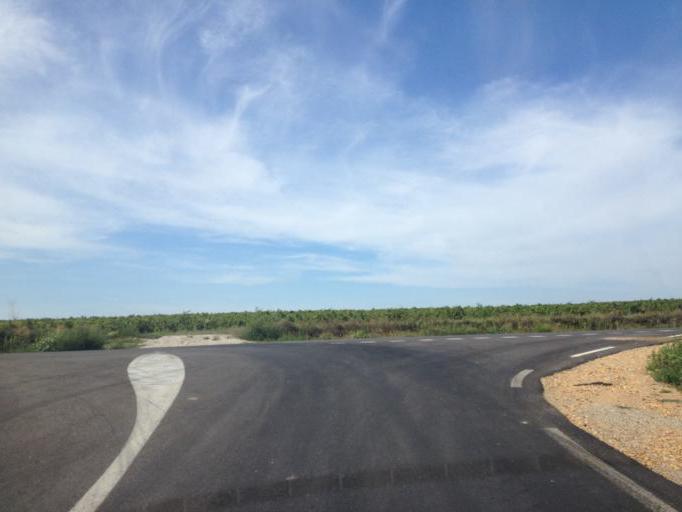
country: FR
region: Provence-Alpes-Cote d'Azur
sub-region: Departement du Vaucluse
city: Courthezon
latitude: 44.0978
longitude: 4.8567
